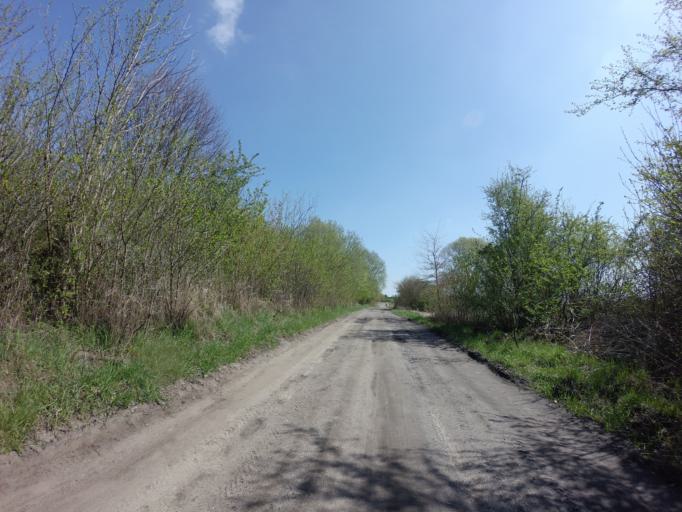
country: PL
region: West Pomeranian Voivodeship
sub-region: Powiat choszczenski
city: Choszczno
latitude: 53.1629
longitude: 15.4459
